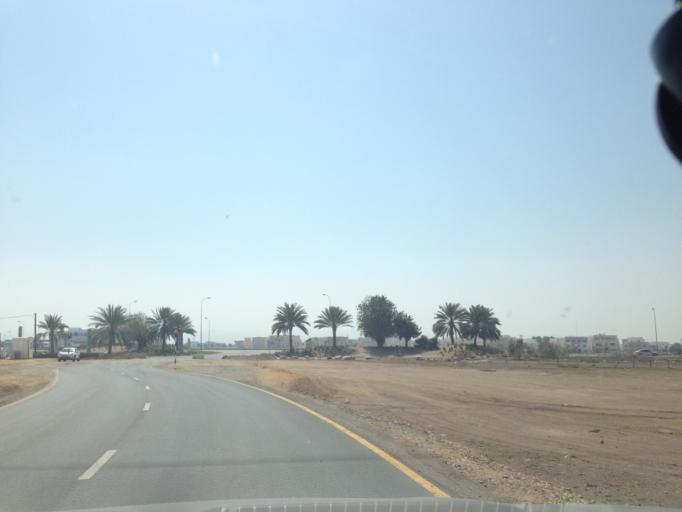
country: OM
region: Muhafazat Masqat
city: As Sib al Jadidah
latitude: 23.6287
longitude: 58.2605
